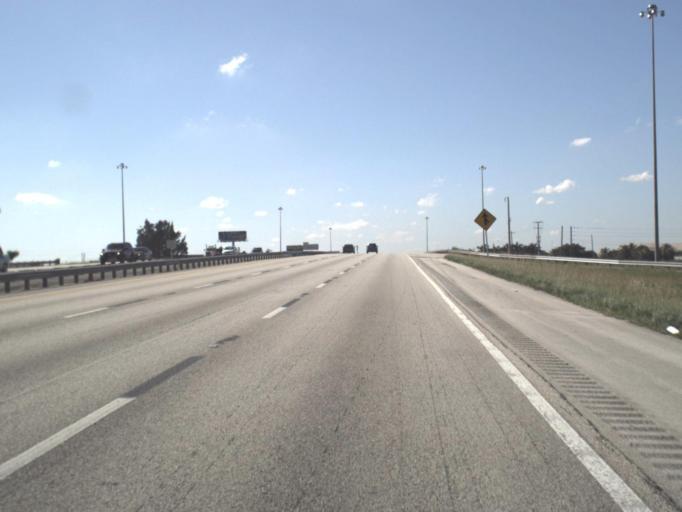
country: US
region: Florida
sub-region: Miami-Dade County
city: Palm Springs North
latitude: 25.9034
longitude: -80.3846
